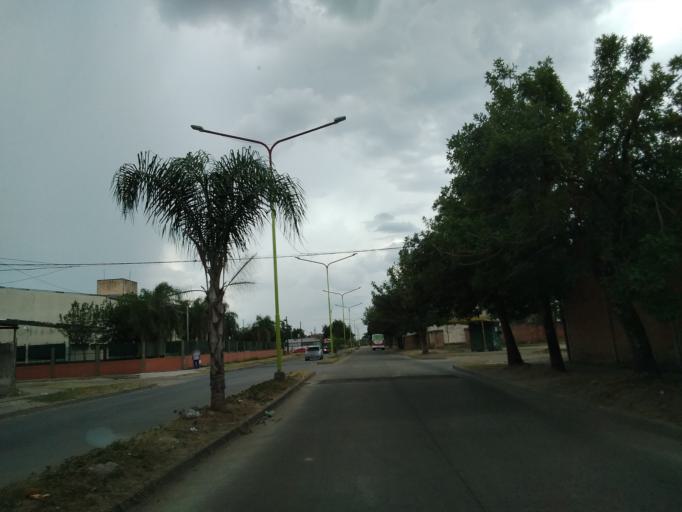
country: AR
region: Corrientes
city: Corrientes
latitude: -27.5231
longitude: -58.7901
